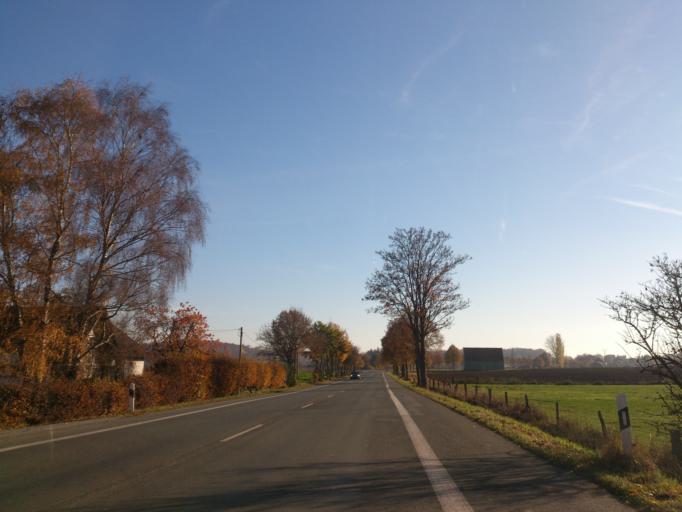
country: DE
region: North Rhine-Westphalia
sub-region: Regierungsbezirk Detmold
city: Willebadessen
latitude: 51.5906
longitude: 9.0357
